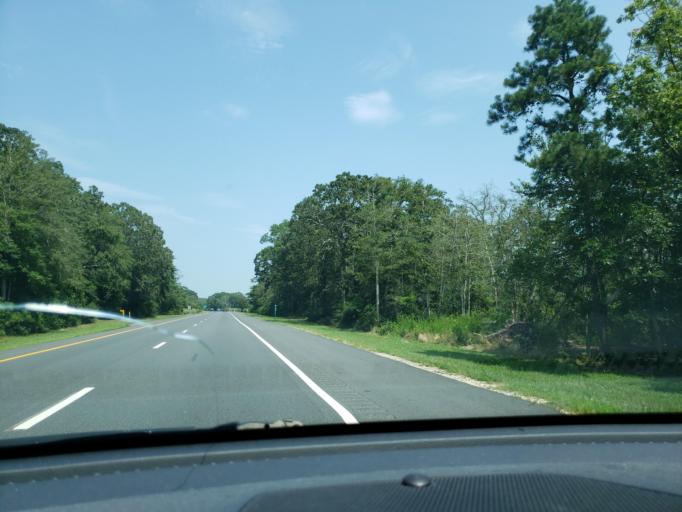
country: US
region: New Jersey
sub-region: Cape May County
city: Ocean City
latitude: 39.2540
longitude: -74.6496
